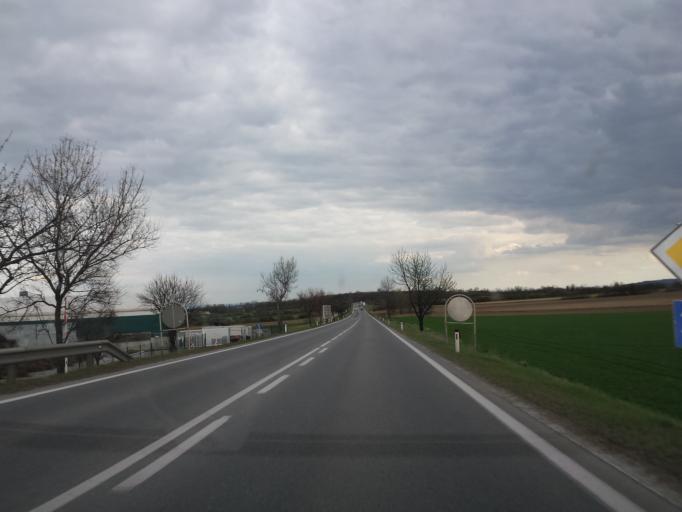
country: AT
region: Lower Austria
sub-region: Politischer Bezirk Krems
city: Stratzing
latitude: 48.4506
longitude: 15.6110
